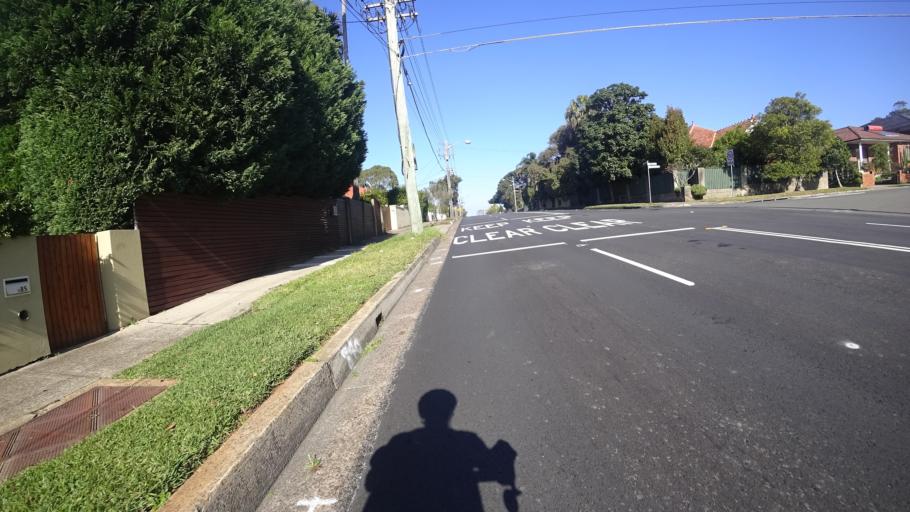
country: AU
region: New South Wales
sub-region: North Sydney
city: St Leonards
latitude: -33.8171
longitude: 151.2054
